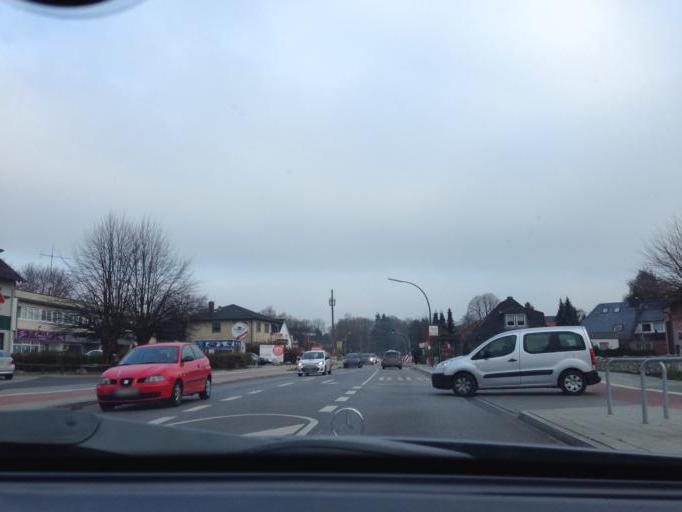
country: DE
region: Hamburg
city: Farmsen-Berne
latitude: 53.6229
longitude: 10.1664
